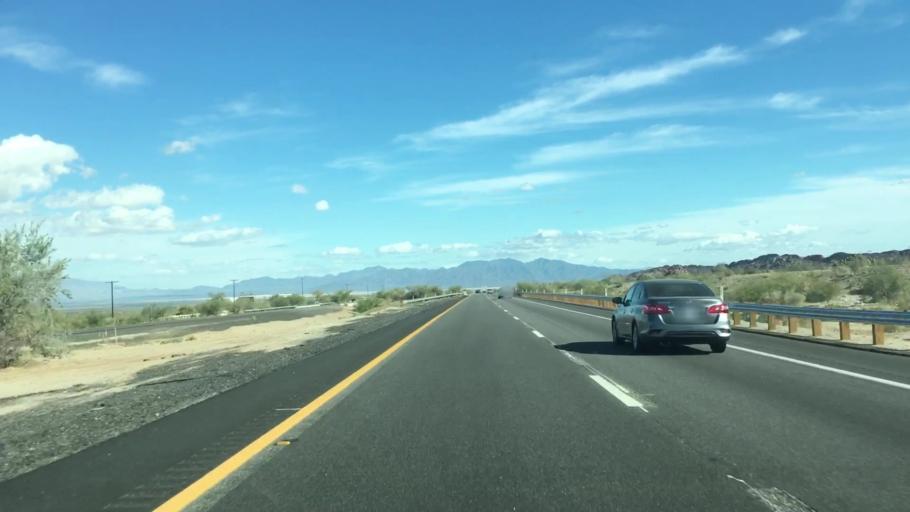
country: US
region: California
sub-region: Imperial County
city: Niland
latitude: 33.7039
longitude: -115.4444
